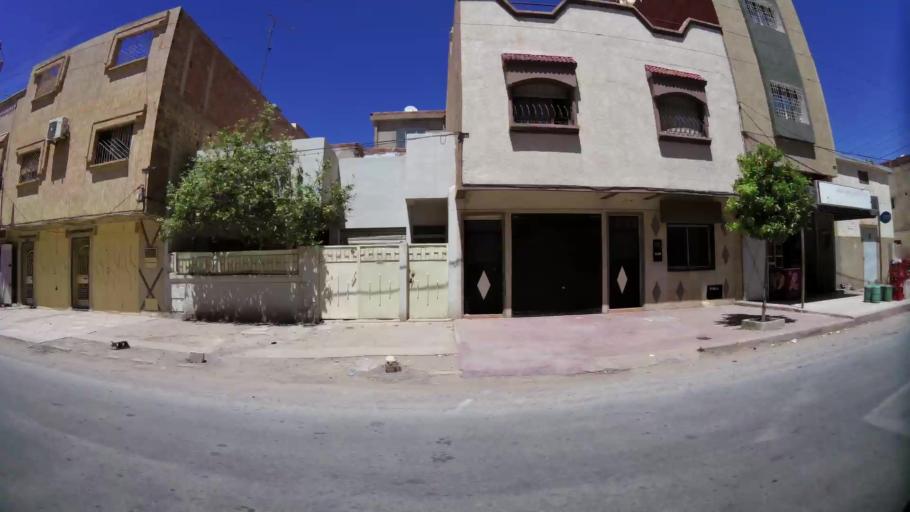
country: MA
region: Oriental
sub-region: Oujda-Angad
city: Oujda
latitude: 34.6571
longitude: -1.9245
